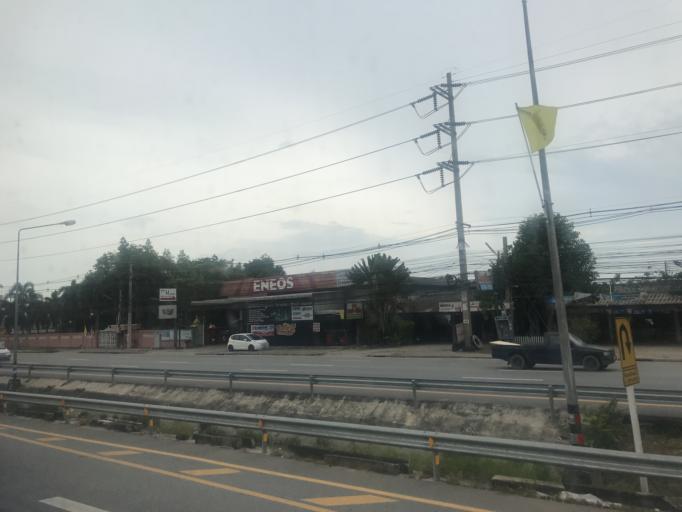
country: TH
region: Chon Buri
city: Bang Lamung
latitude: 13.0165
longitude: 100.9316
